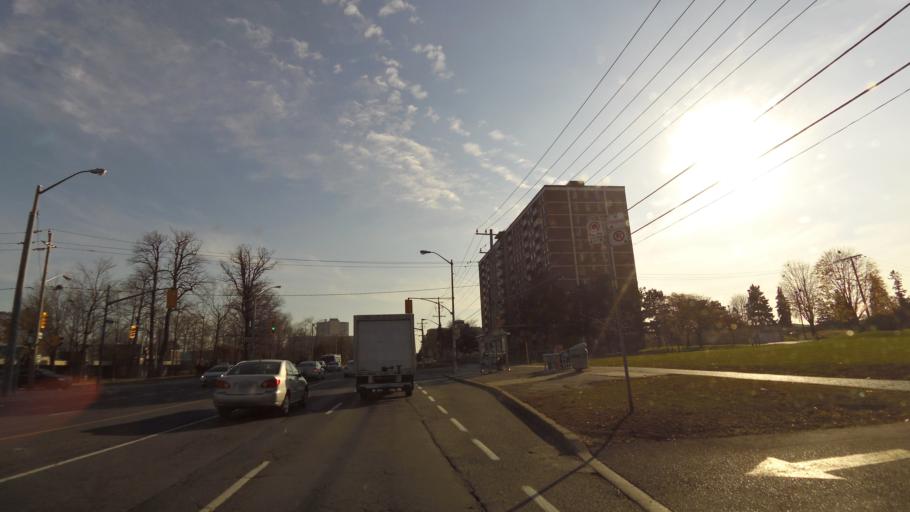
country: CA
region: Ontario
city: Concord
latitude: 43.7663
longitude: -79.5198
